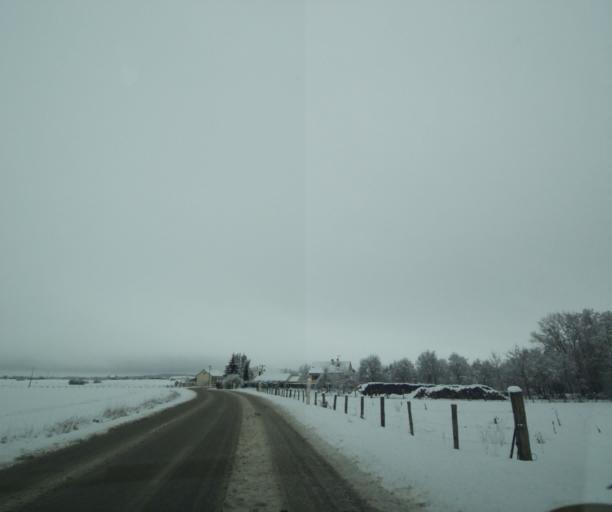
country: FR
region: Champagne-Ardenne
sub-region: Departement de la Haute-Marne
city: Wassy
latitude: 48.5317
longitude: 4.9256
